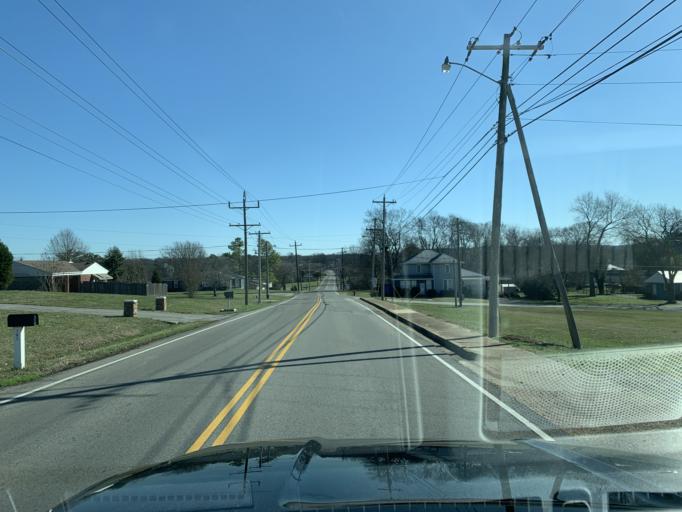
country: US
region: Tennessee
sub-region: Maury County
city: Mount Pleasant
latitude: 35.5415
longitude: -87.2142
